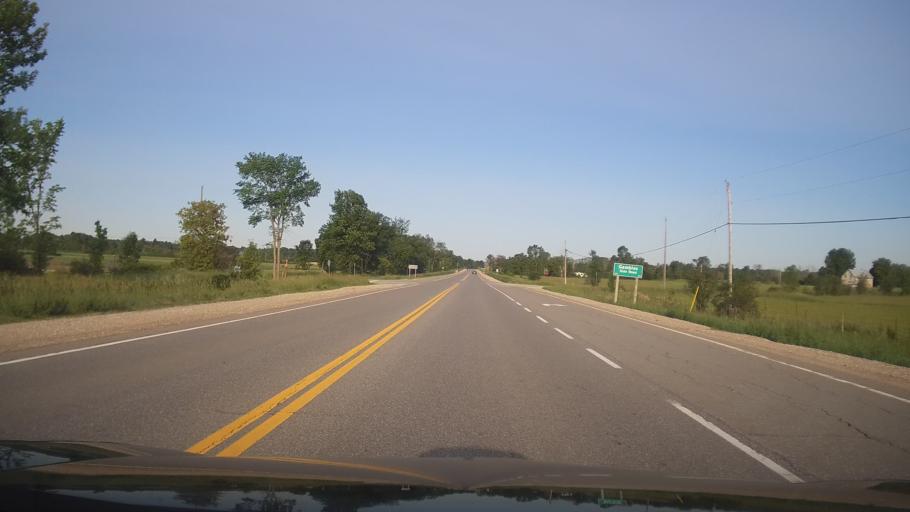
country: CA
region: Ontario
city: Perth
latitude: 44.8715
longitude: -76.3743
